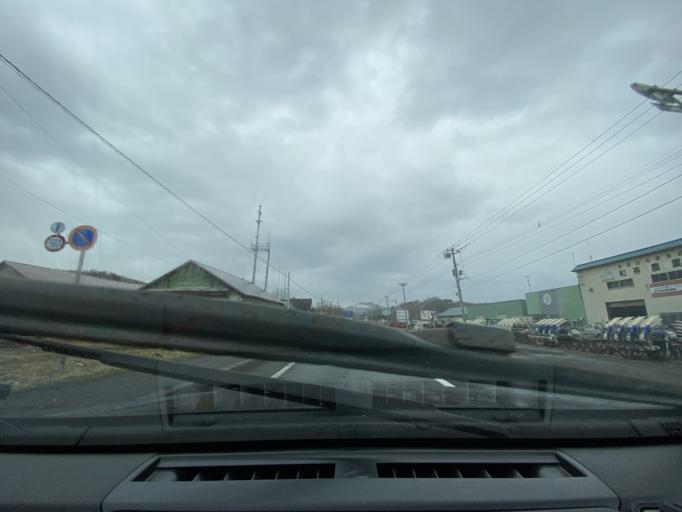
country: JP
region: Hokkaido
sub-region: Asahikawa-shi
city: Asahikawa
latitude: 44.0208
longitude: 142.4189
